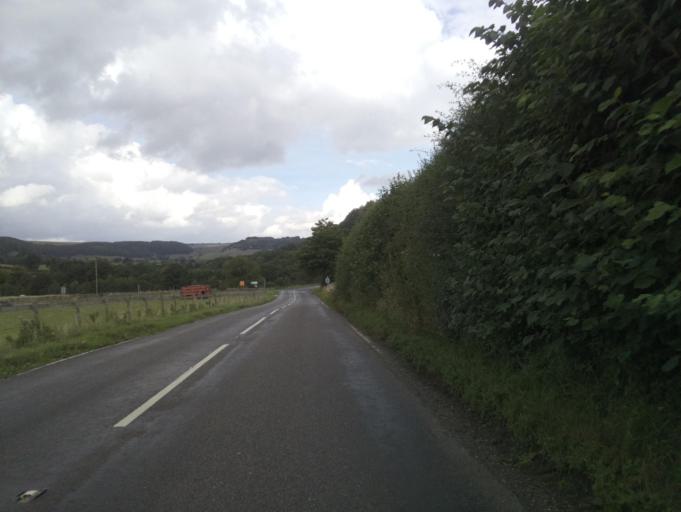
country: GB
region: England
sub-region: North Yorkshire
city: Leyburn
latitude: 54.3845
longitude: -1.8296
